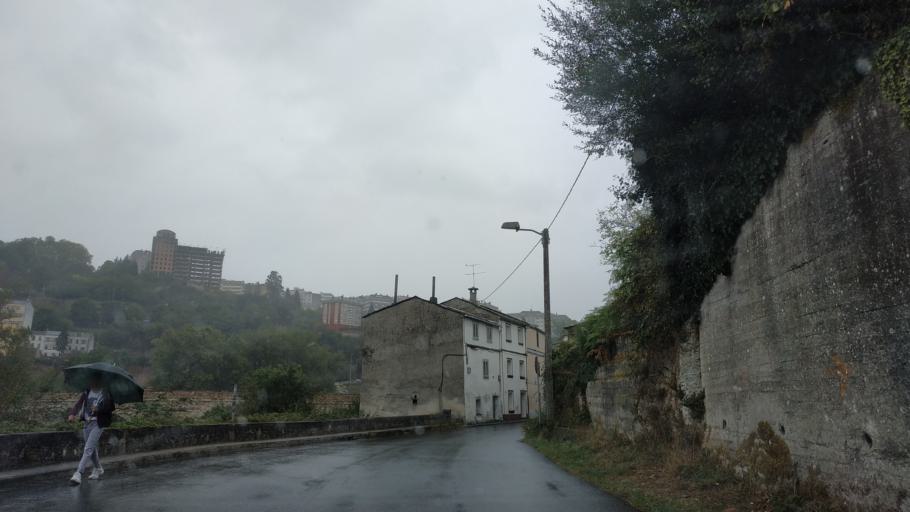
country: ES
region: Galicia
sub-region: Provincia de Lugo
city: Lugo
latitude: 43.0013
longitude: -7.5645
